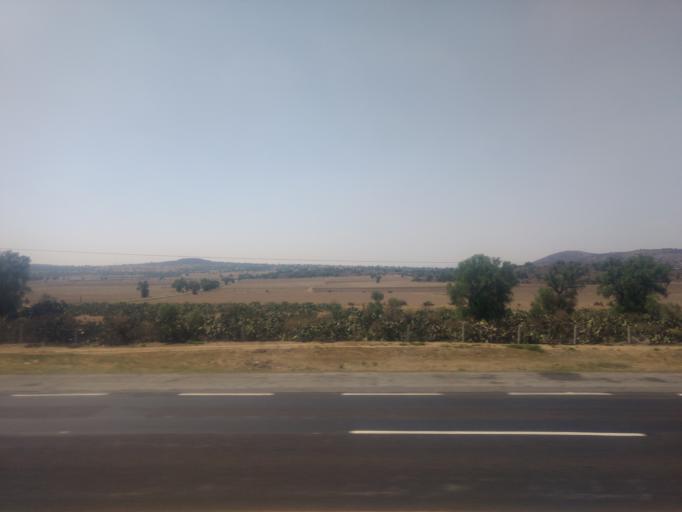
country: MX
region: Morelos
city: Nopaltepec
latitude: 19.8095
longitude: -98.7198
